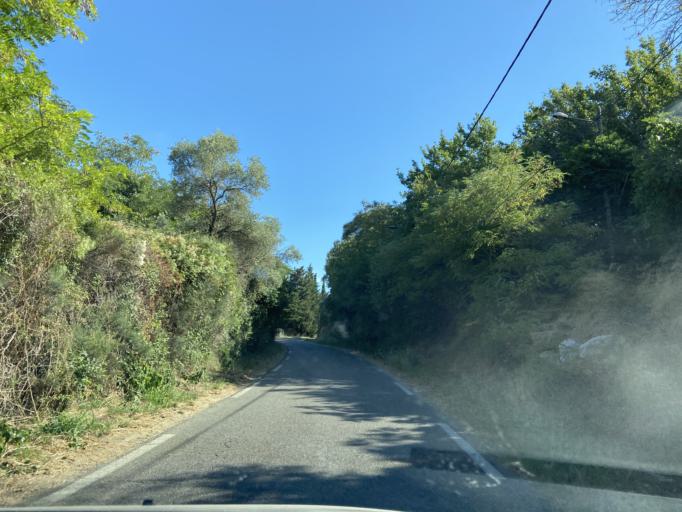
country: FR
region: Provence-Alpes-Cote d'Azur
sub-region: Departement des Bouches-du-Rhone
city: Saint-Chamas
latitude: 43.5621
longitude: 5.0265
